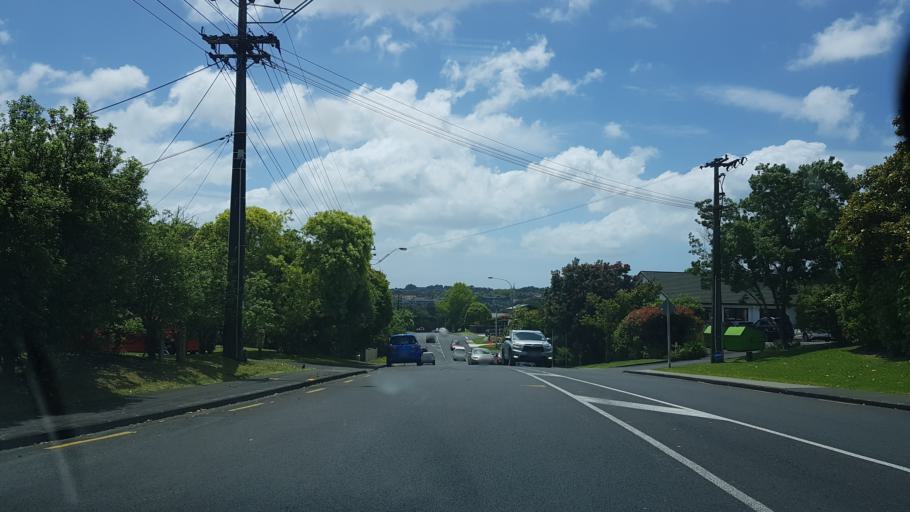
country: NZ
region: Auckland
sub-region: Auckland
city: North Shore
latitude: -36.7879
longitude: 174.6997
